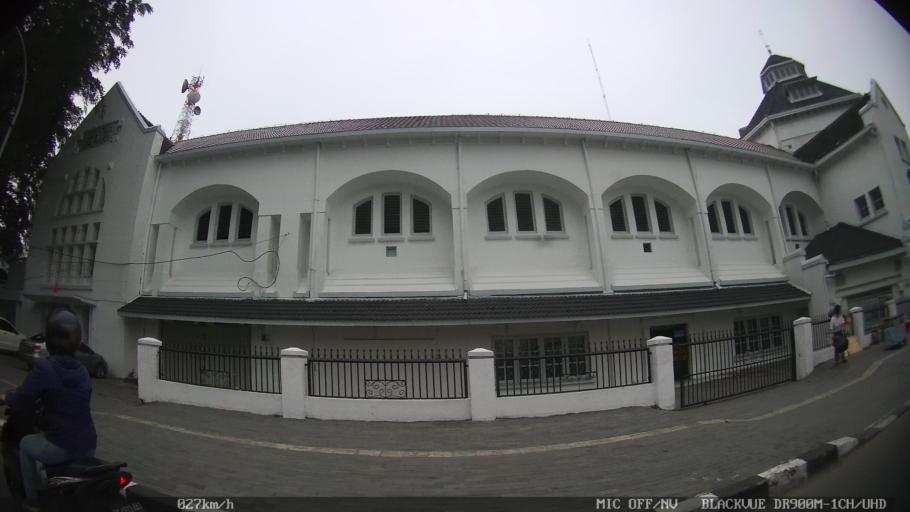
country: ID
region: North Sumatra
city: Medan
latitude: 3.5917
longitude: 98.6771
